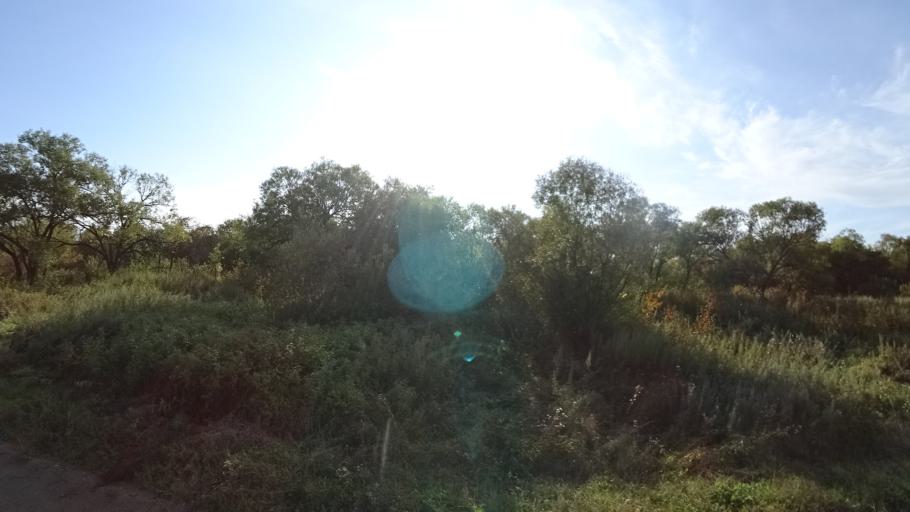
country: RU
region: Amur
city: Arkhara
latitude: 49.3508
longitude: 130.1006
